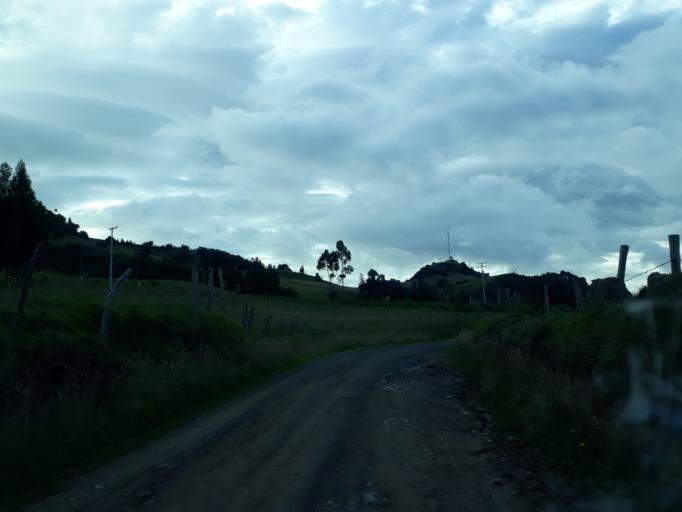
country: CO
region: Cundinamarca
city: Carmen de Carupa
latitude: 5.3233
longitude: -73.9123
